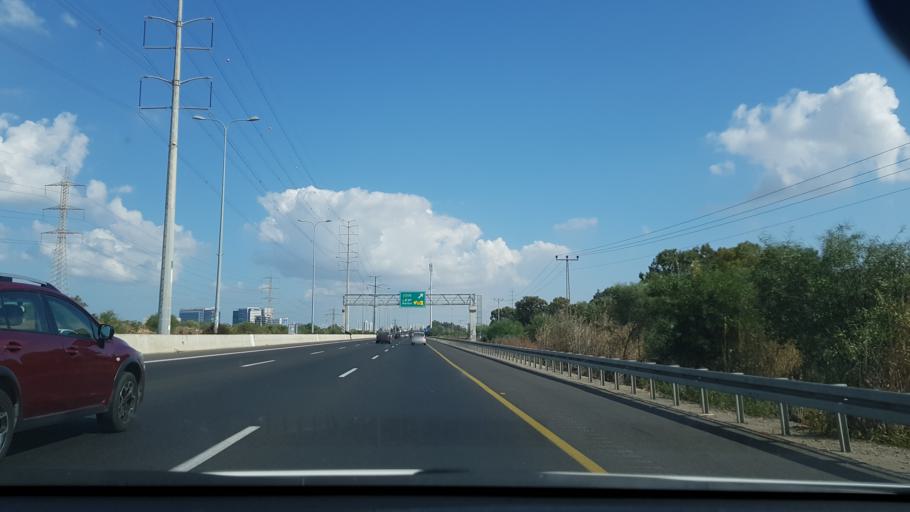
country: IL
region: Central District
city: Rishon LeZiyyon
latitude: 31.9905
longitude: 34.7981
